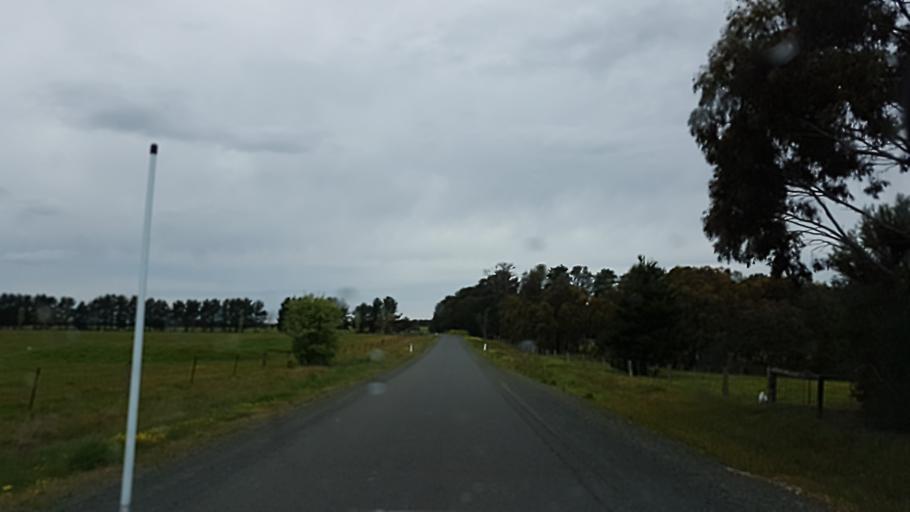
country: AU
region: Victoria
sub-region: Ballarat North
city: Mount Clear
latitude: -37.7742
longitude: 144.0875
